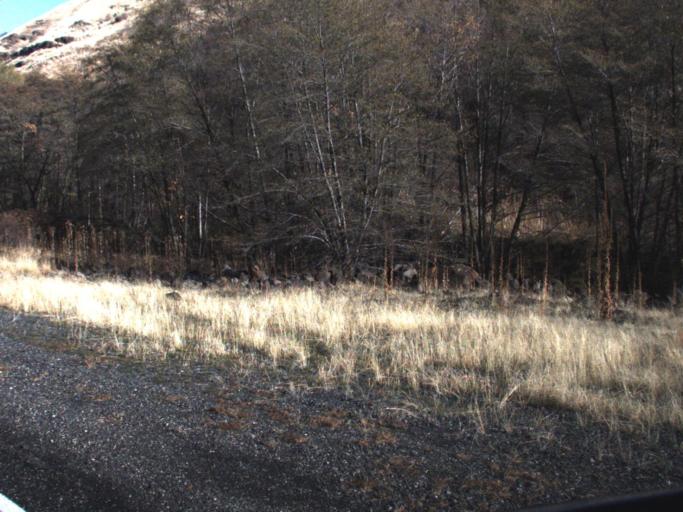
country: US
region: Washington
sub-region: Asotin County
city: Asotin
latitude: 46.0208
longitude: -117.2633
